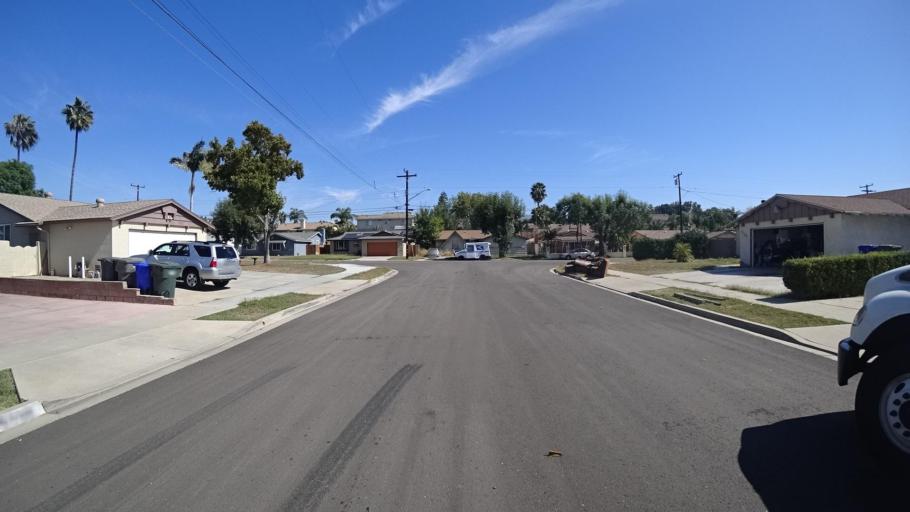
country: US
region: California
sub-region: San Diego County
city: La Presa
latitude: 32.7107
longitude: -117.0097
